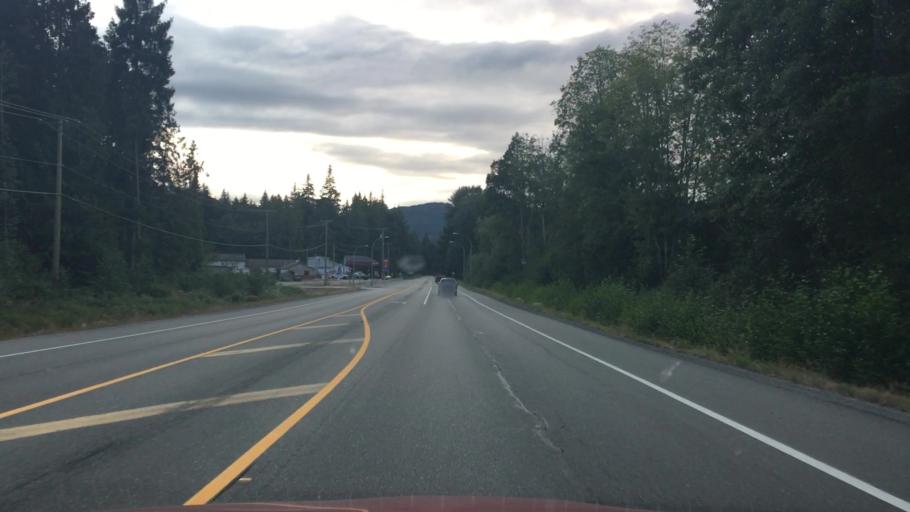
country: CA
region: British Columbia
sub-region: Regional District of Nanaimo
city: Parksville
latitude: 49.3120
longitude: -124.5157
